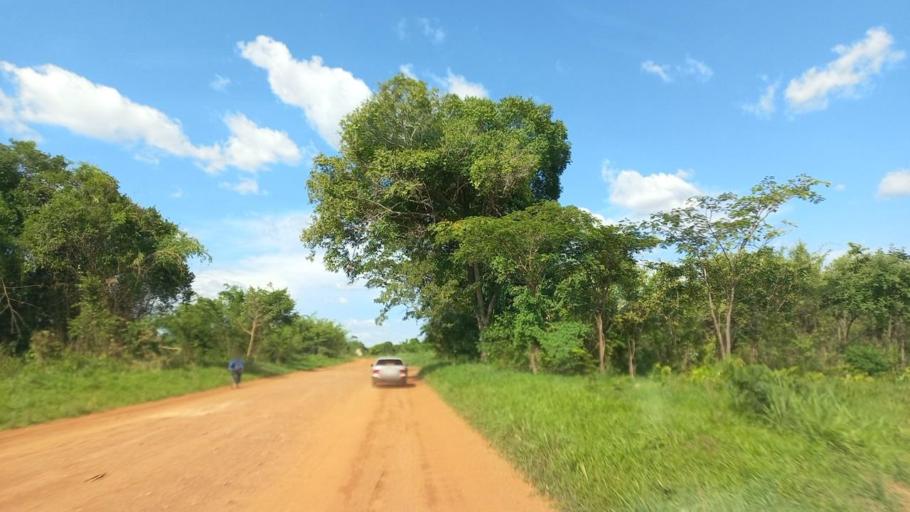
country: ZM
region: Copperbelt
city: Kitwe
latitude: -12.8612
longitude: 28.3829
